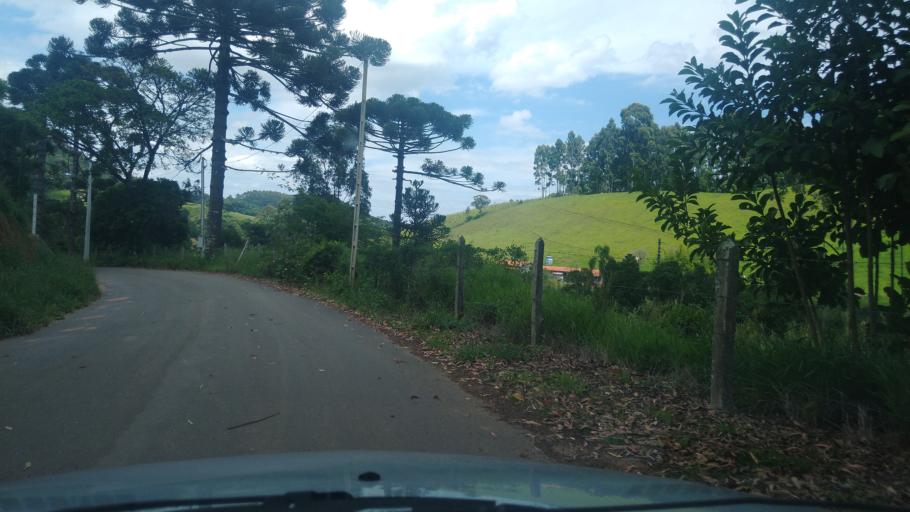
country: BR
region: Minas Gerais
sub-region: Extrema
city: Extrema
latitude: -22.7276
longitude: -46.3119
